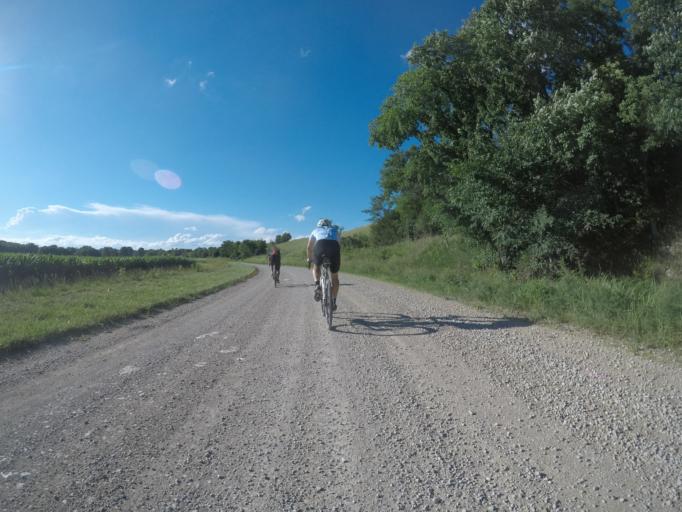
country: US
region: Kansas
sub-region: Riley County
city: Ogden
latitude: 39.2411
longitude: -96.7311
